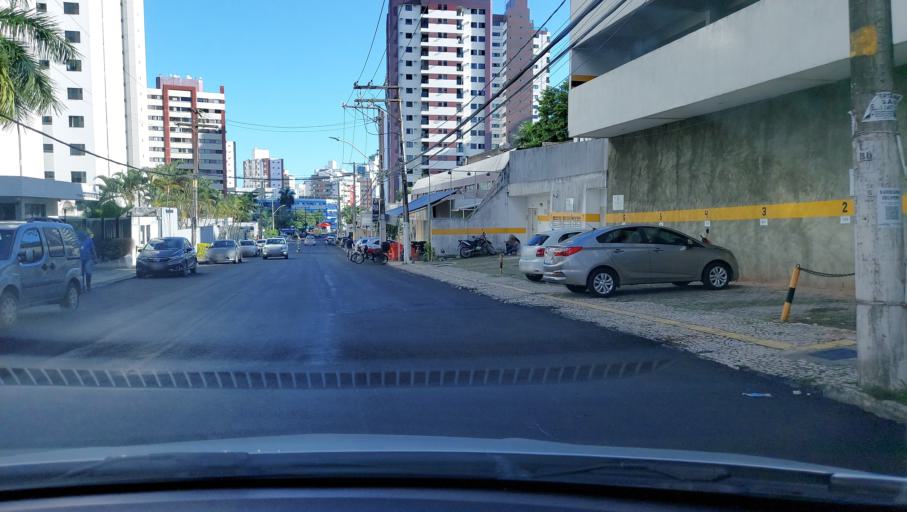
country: BR
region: Bahia
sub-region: Salvador
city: Salvador
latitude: -12.9872
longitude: -38.4539
